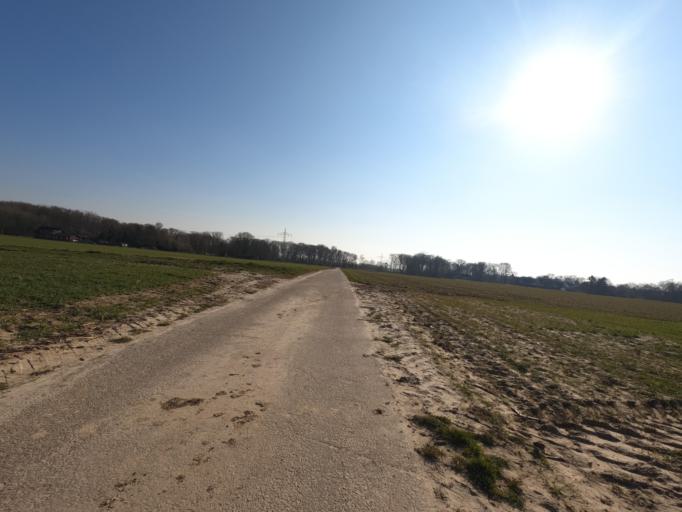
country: DE
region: North Rhine-Westphalia
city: Erkelenz
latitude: 51.0571
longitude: 6.3222
